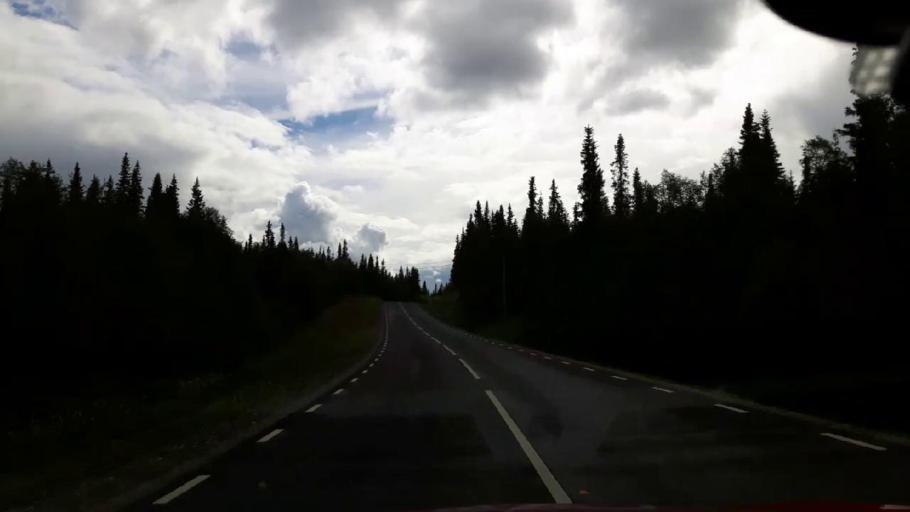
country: NO
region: Nord-Trondelag
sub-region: Royrvik
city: Royrvik
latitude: 64.8142
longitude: 14.0637
